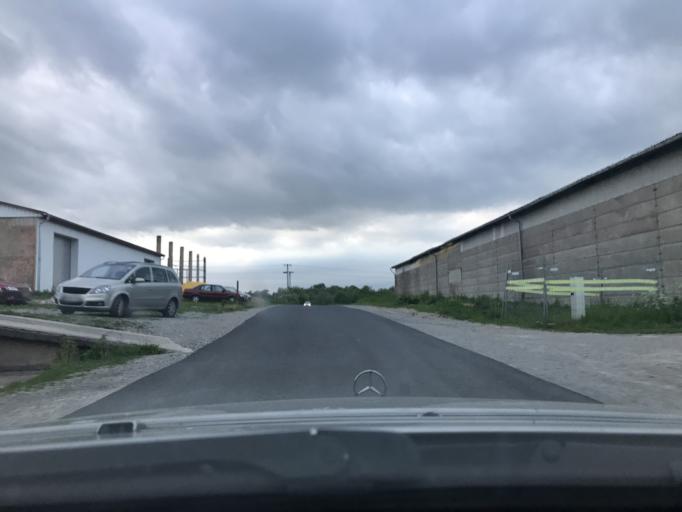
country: DE
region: Thuringia
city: Oberdorla
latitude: 51.2143
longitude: 10.3992
